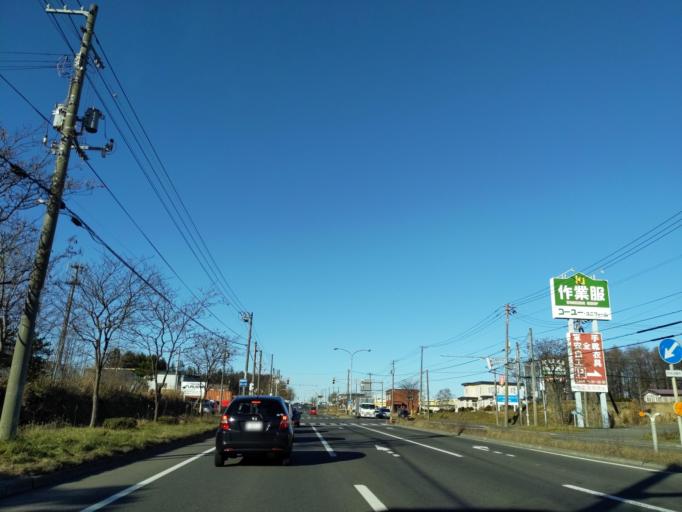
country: JP
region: Hokkaido
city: Kitahiroshima
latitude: 42.9428
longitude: 141.5031
